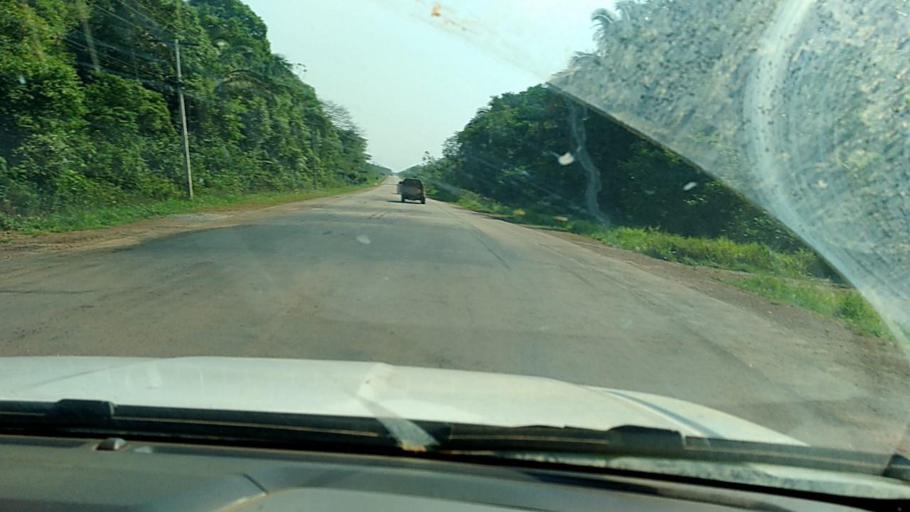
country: BR
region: Amazonas
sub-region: Humaita
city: Humaita
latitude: -7.7922
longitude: -63.1612
